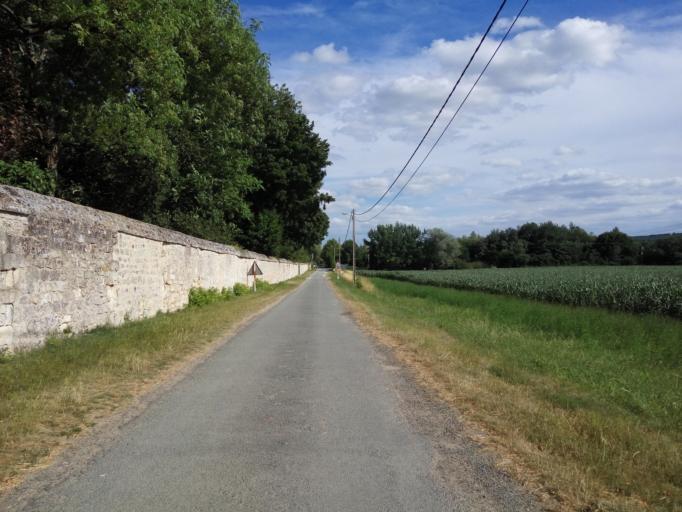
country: FR
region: Picardie
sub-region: Departement de l'Oise
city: Boran-sur-Oise
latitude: 49.1596
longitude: 2.3516
